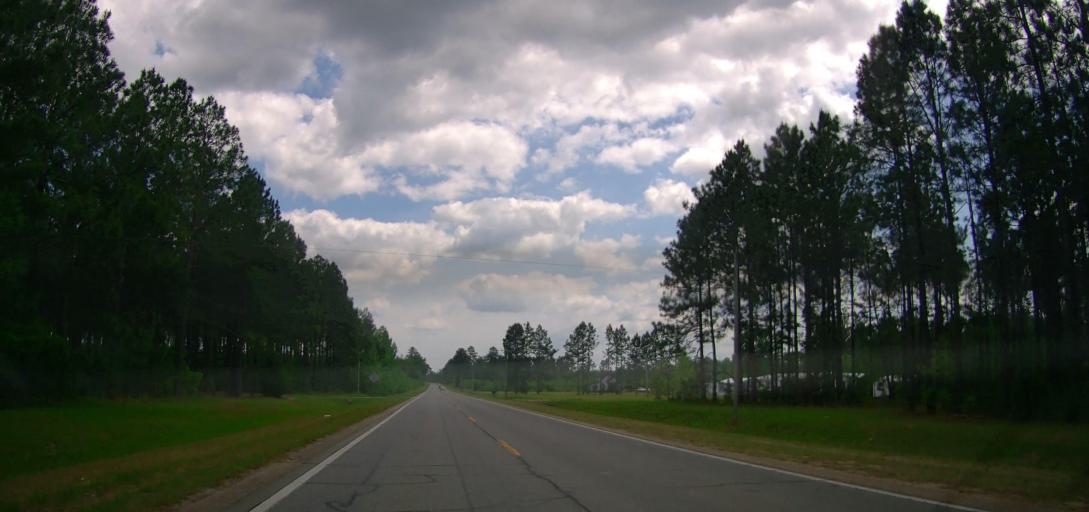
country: US
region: Georgia
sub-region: Laurens County
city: East Dublin
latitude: 32.4979
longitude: -82.8316
